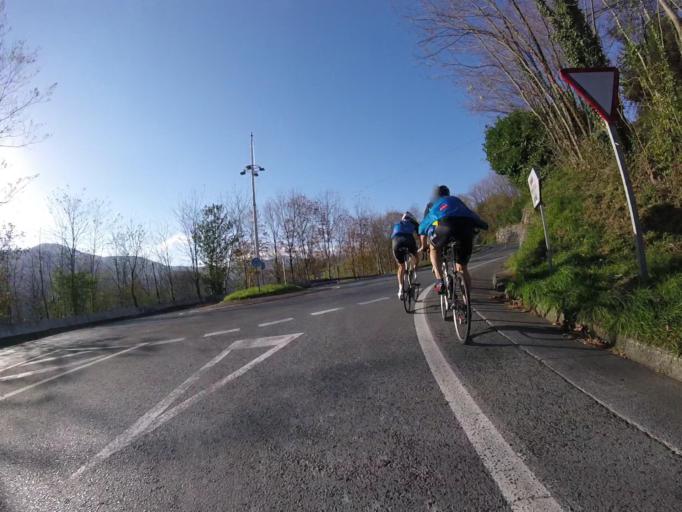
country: ES
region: Navarre
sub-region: Provincia de Navarra
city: Igantzi
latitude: 43.2238
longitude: -1.6949
